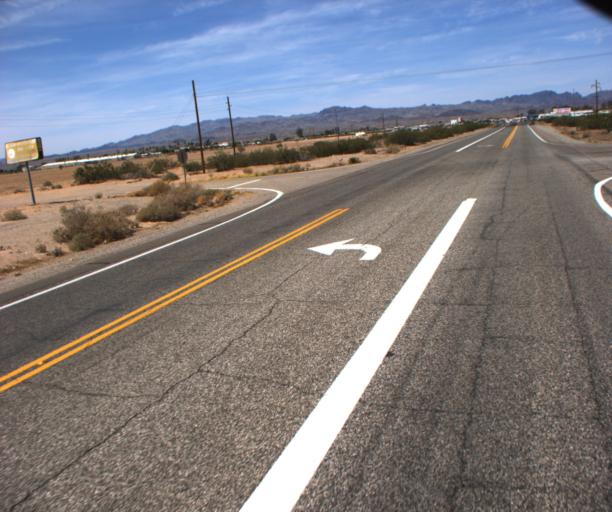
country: US
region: Arizona
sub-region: La Paz County
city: Parker
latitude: 34.1293
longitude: -114.2796
